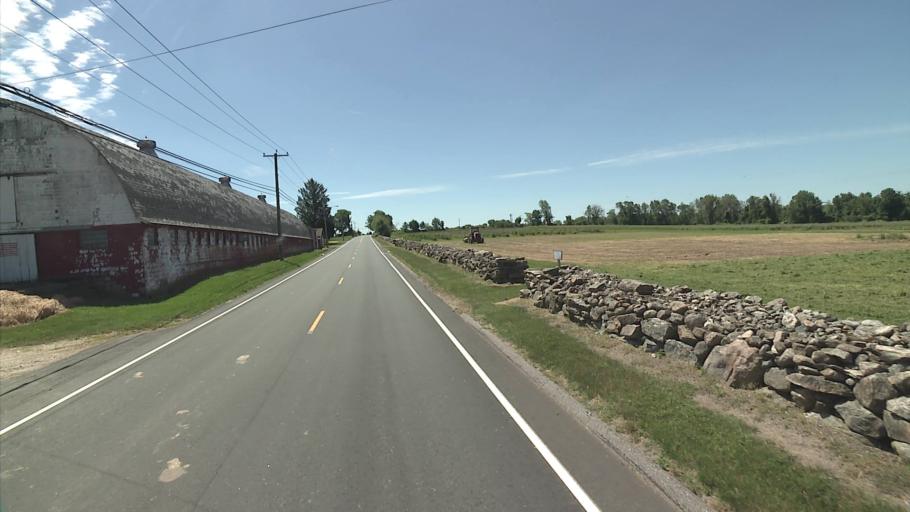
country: US
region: Connecticut
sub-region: Windham County
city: Moosup
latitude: 41.6734
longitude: -71.8505
